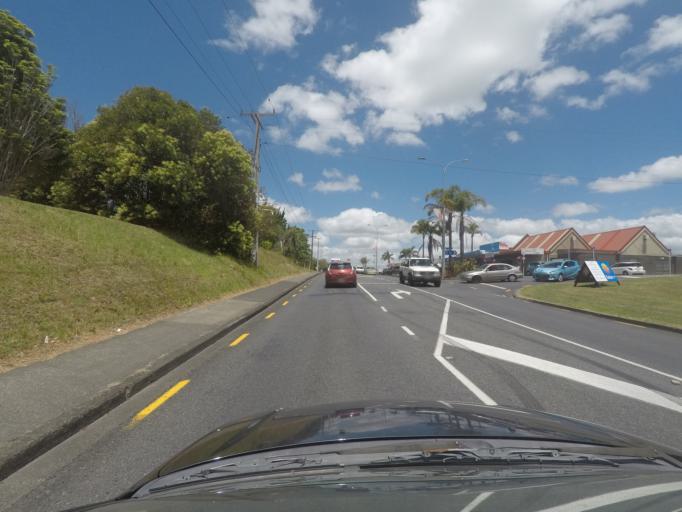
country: NZ
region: Northland
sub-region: Whangarei
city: Whangarei
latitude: -35.7541
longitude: 174.3684
